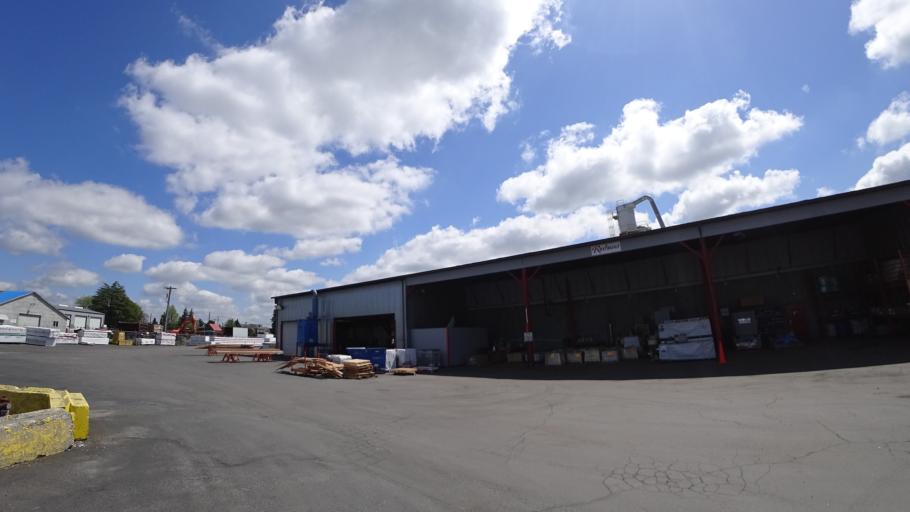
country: US
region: Oregon
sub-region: Washington County
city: Hillsboro
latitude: 45.5162
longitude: -122.9928
